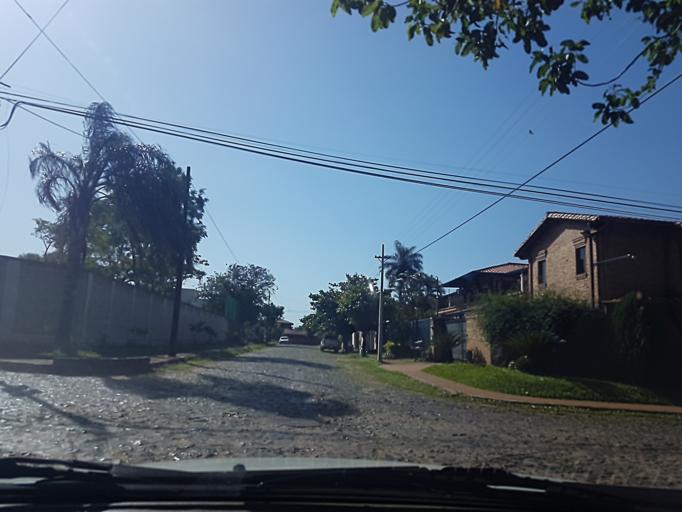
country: PY
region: Asuncion
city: Asuncion
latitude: -25.2685
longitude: -57.5668
